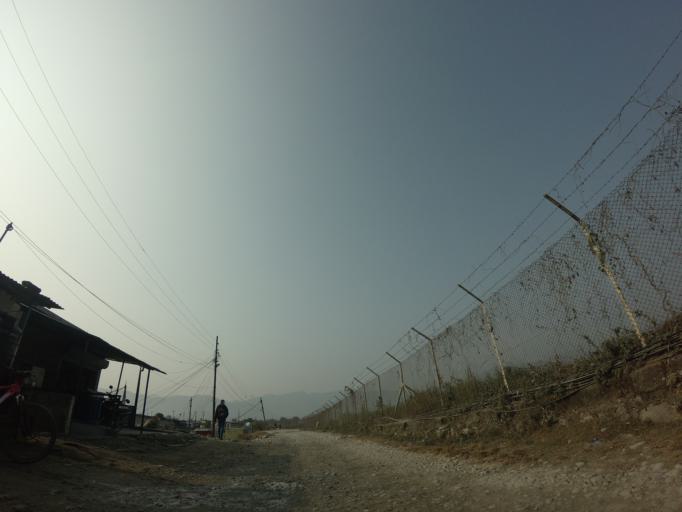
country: NP
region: Western Region
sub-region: Gandaki Zone
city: Pokhara
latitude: 28.2035
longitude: 83.9862
